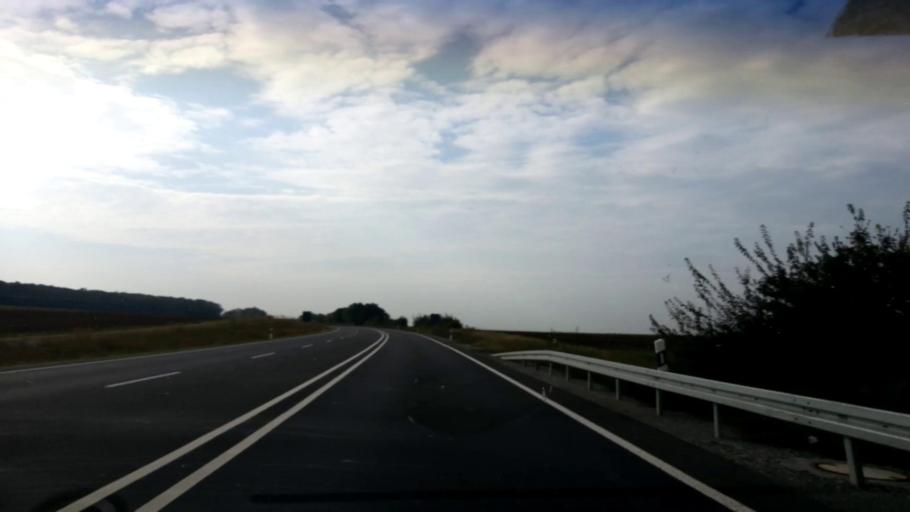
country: DE
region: Bavaria
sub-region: Regierungsbezirk Unterfranken
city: Gerolzhofen
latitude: 49.8885
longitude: 10.3562
